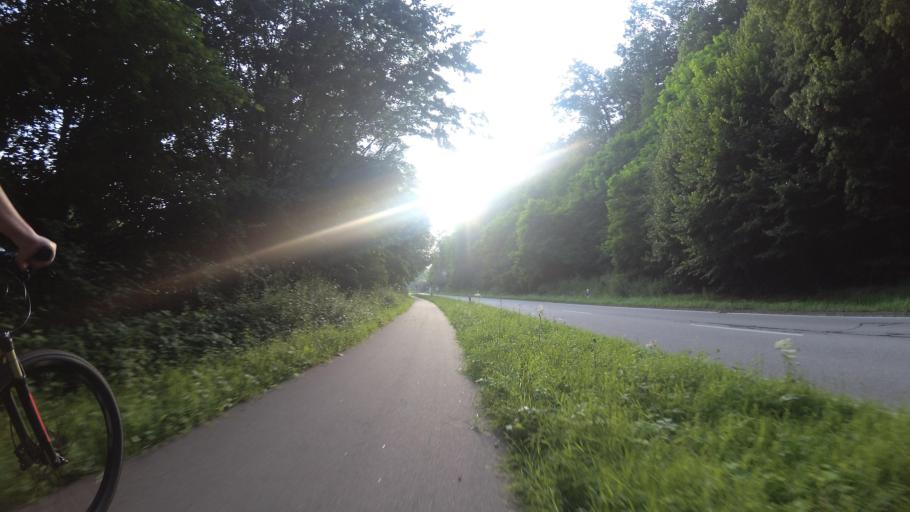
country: DE
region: Rheinland-Pfalz
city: Zweibrucken
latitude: 49.2259
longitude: 7.3715
